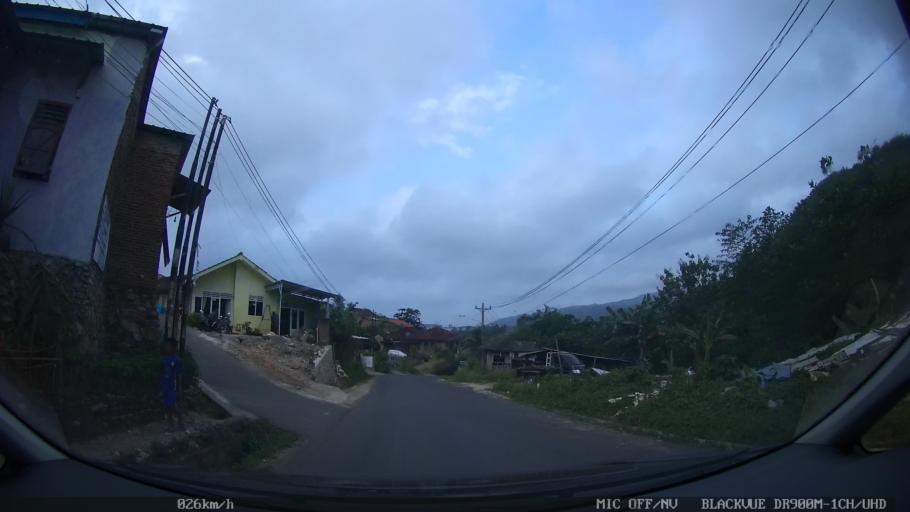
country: ID
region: Lampung
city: Bandarlampung
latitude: -5.4222
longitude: 105.2841
